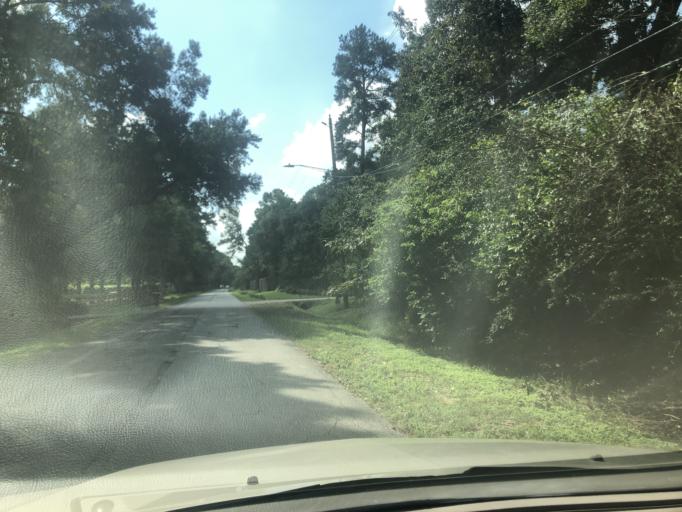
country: US
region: Texas
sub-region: Harris County
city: Bunker Hill Village
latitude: 29.7458
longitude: -95.5459
